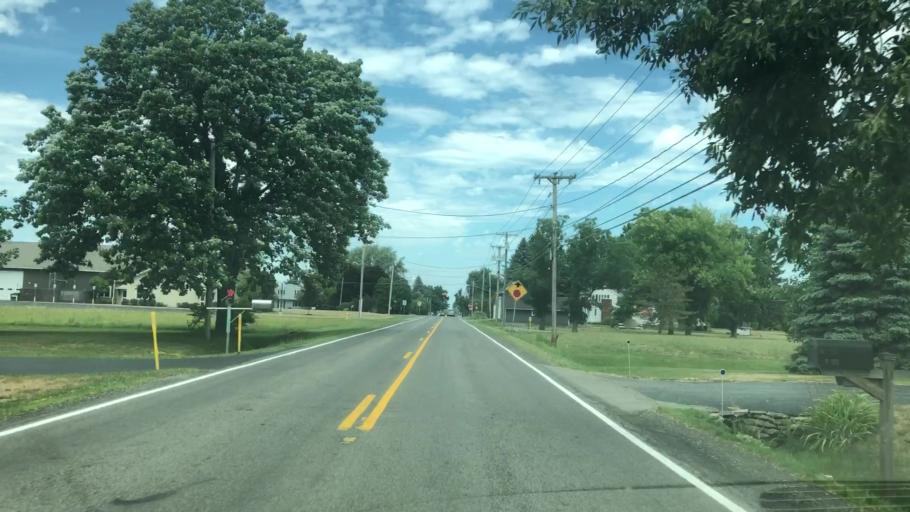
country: US
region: New York
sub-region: Monroe County
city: Webster
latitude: 43.1801
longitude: -77.4004
